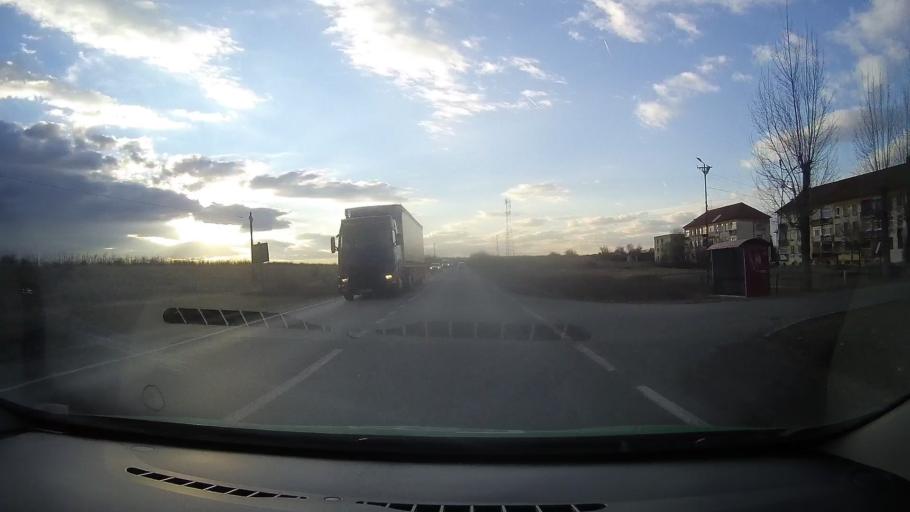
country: RO
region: Dambovita
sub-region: Comuna I. L. Caragiale
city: Mija
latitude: 44.9126
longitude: 25.6758
